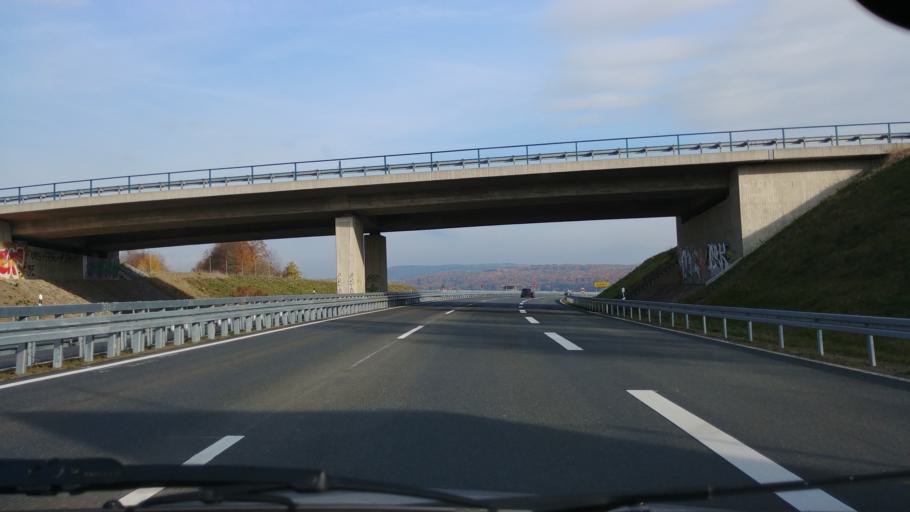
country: DE
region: Hesse
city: Merenberg
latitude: 50.4757
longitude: 8.1475
